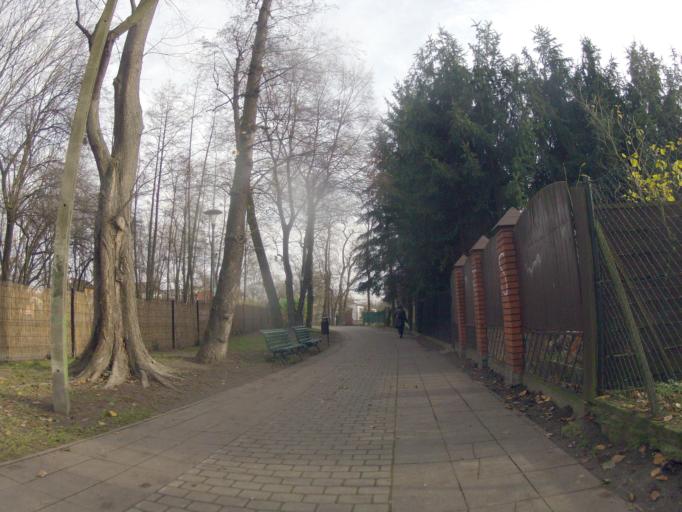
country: PL
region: Lesser Poland Voivodeship
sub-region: Krakow
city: Krakow
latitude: 50.0738
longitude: 19.8973
